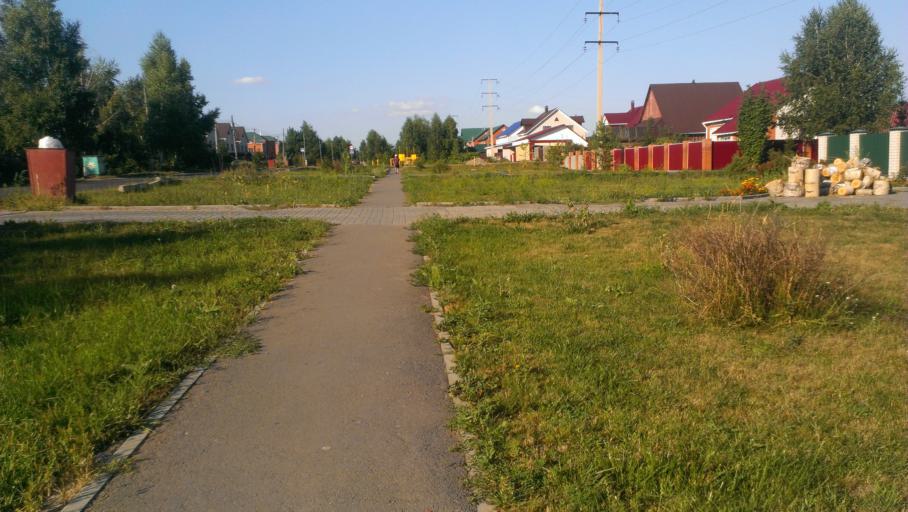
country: RU
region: Altai Krai
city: Novosilikatnyy
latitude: 53.3587
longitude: 83.6392
